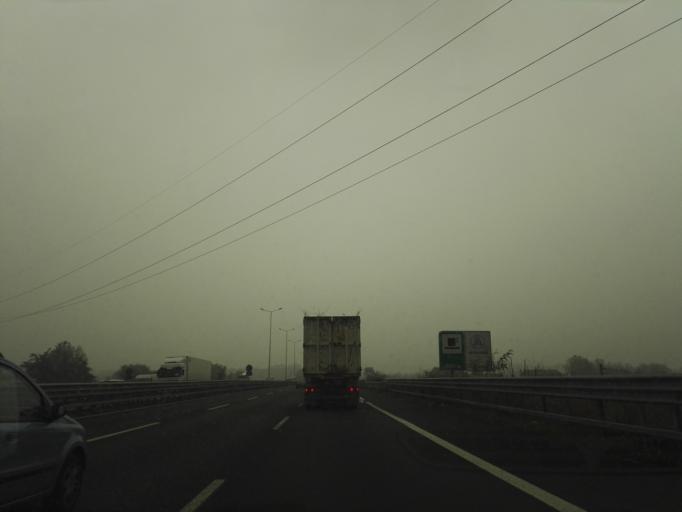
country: IT
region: Lombardy
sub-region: Citta metropolitana di Milano
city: Settimo Milanese
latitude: 45.4617
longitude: 9.0764
